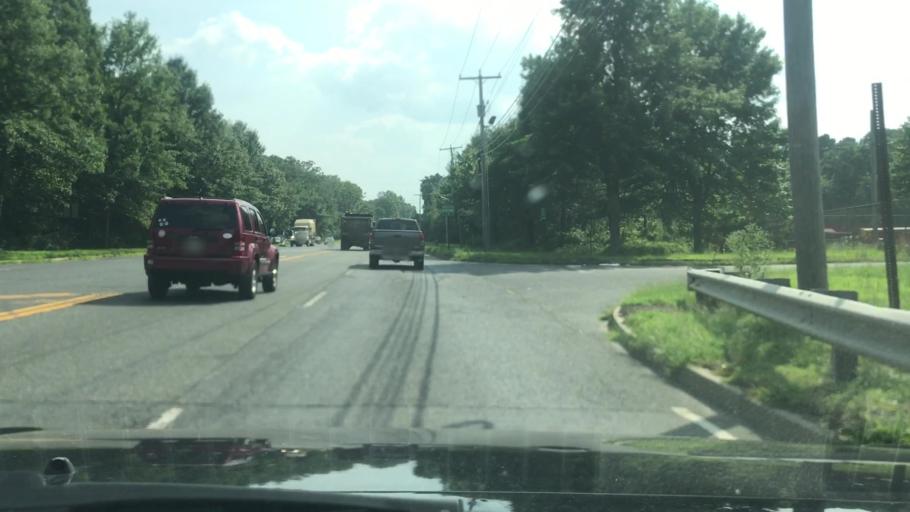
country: US
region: New Jersey
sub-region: Monmouth County
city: Tinton Falls
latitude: 40.2445
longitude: -74.1024
